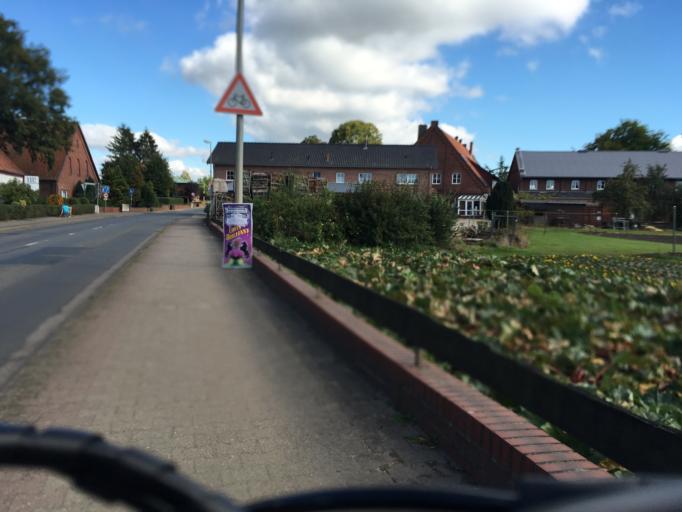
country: DE
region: Lower Saxony
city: Bardowick
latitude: 53.2997
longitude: 10.3955
